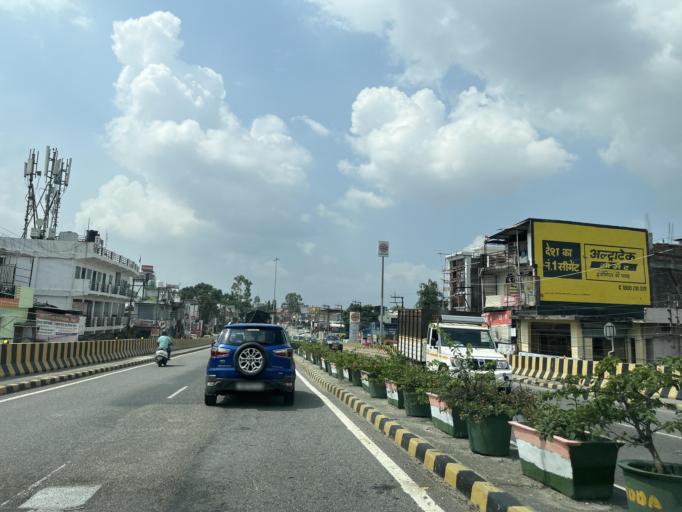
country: IN
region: Uttarakhand
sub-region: Dehradun
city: Raipur
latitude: 30.2788
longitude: 78.0733
